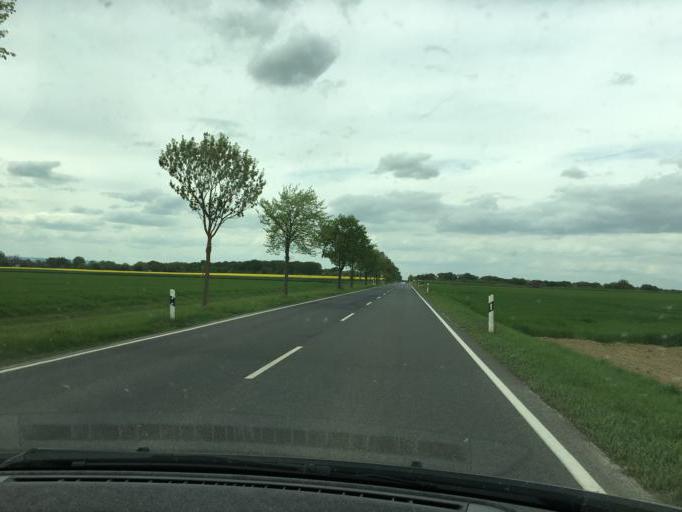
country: DE
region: North Rhine-Westphalia
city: Zulpich
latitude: 50.7232
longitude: 6.6836
